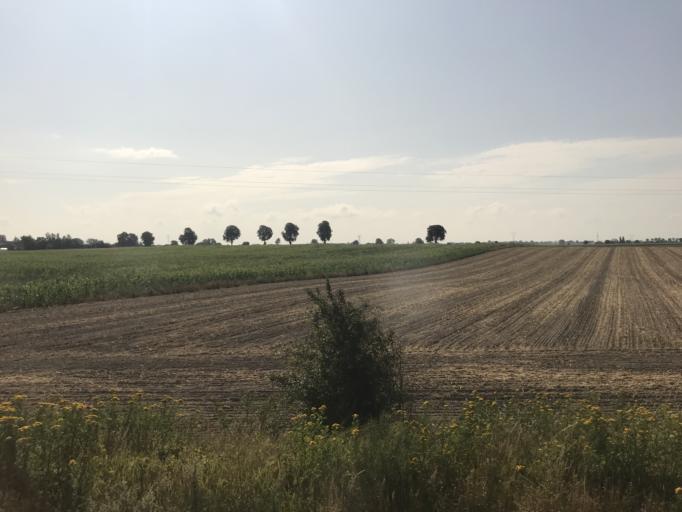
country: PL
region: Kujawsko-Pomorskie
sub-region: Powiat swiecki
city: Pruszcz
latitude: 53.3119
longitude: 18.1636
